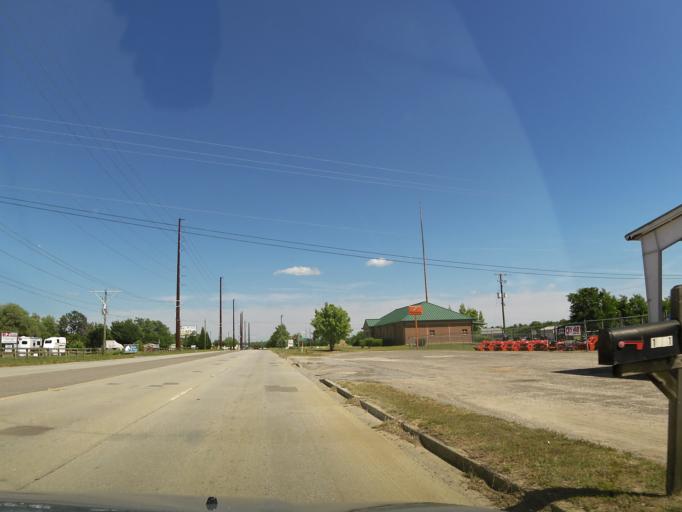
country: US
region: South Carolina
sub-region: Aiken County
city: Aiken
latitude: 33.5526
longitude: -81.6954
